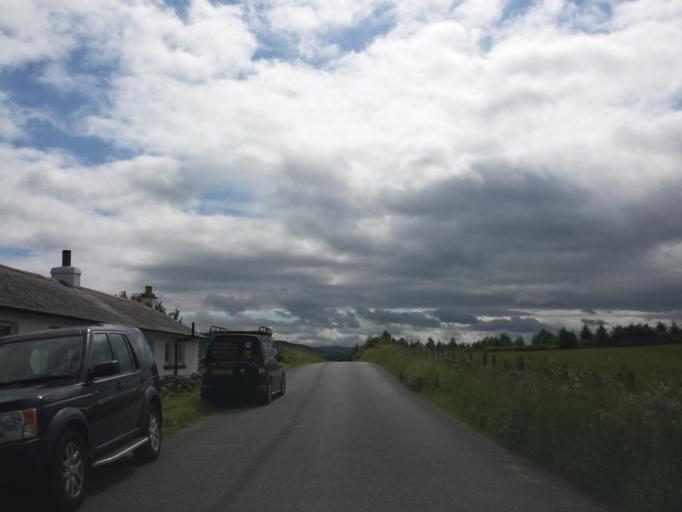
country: GB
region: Scotland
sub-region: Highland
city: Fortrose
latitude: 57.4787
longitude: -4.0853
